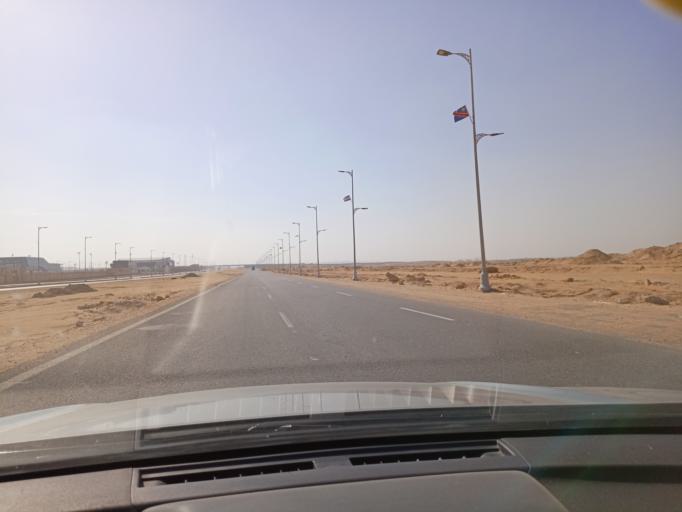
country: EG
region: Muhafazat al Qalyubiyah
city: Al Khankah
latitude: 30.0444
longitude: 31.7010
